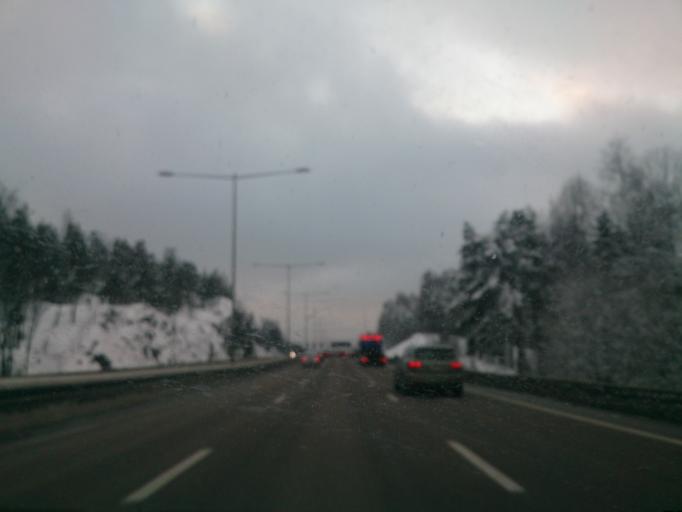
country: SE
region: Stockholm
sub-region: Salems Kommun
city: Ronninge
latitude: 59.2094
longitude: 17.7147
